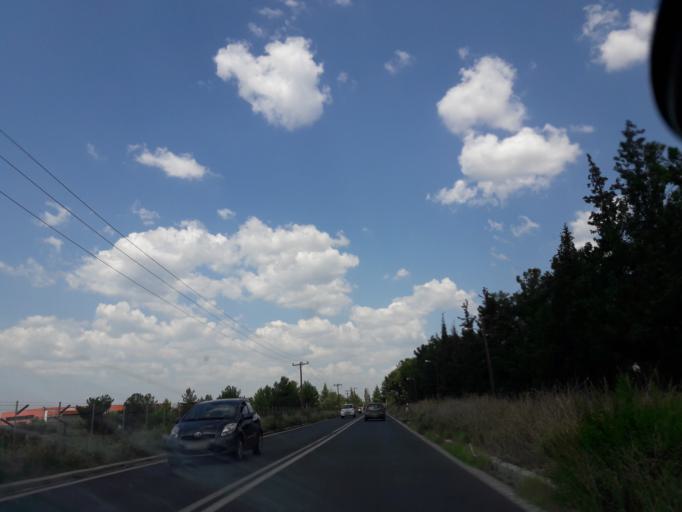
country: GR
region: Central Macedonia
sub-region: Nomos Thessalonikis
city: Thermi
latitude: 40.5357
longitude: 23.0365
